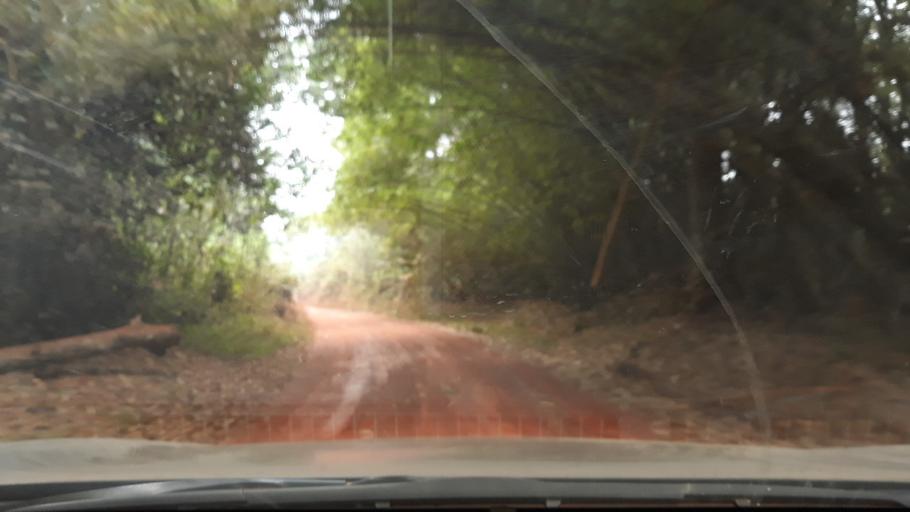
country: CD
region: Eastern Province
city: Buta
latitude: 2.2986
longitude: 25.0476
